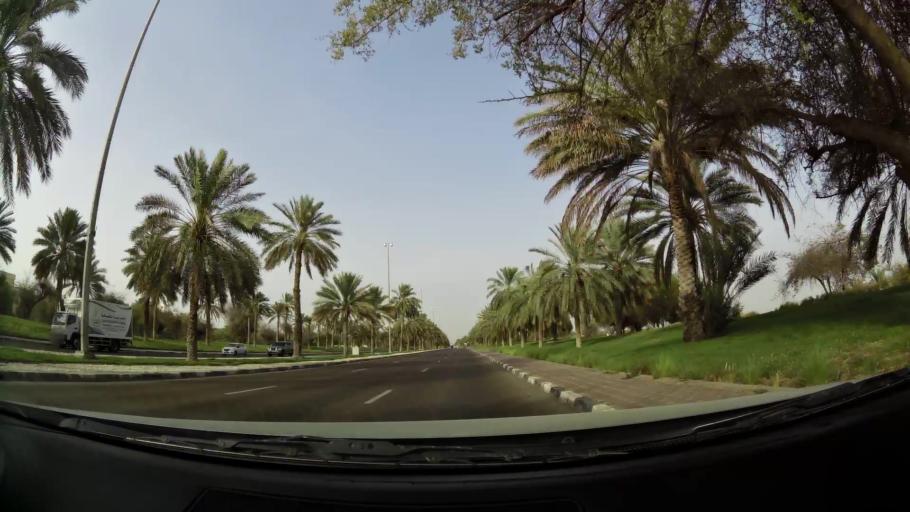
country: AE
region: Abu Dhabi
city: Al Ain
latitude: 24.2239
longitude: 55.7034
